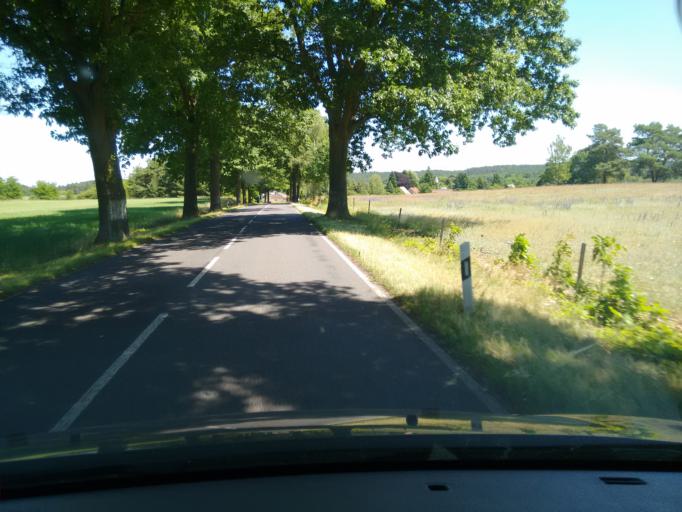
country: DE
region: Brandenburg
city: Gross Lindow
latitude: 52.1878
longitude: 14.5244
